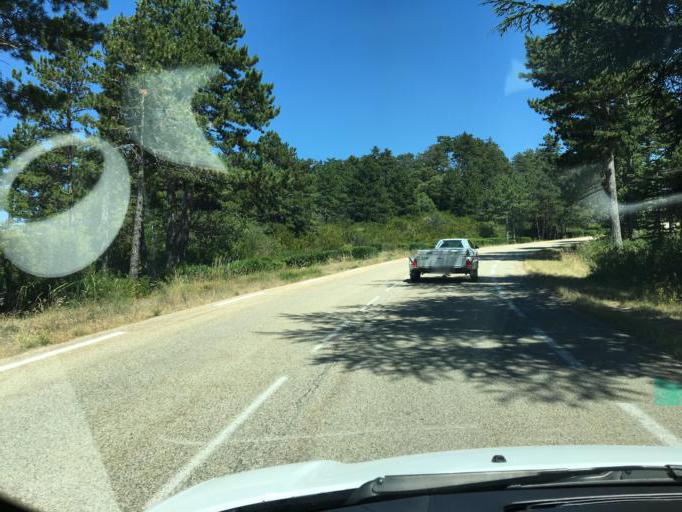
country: FR
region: Provence-Alpes-Cote d'Azur
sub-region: Departement du Vaucluse
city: Bedoin
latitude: 44.1675
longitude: 5.1766
